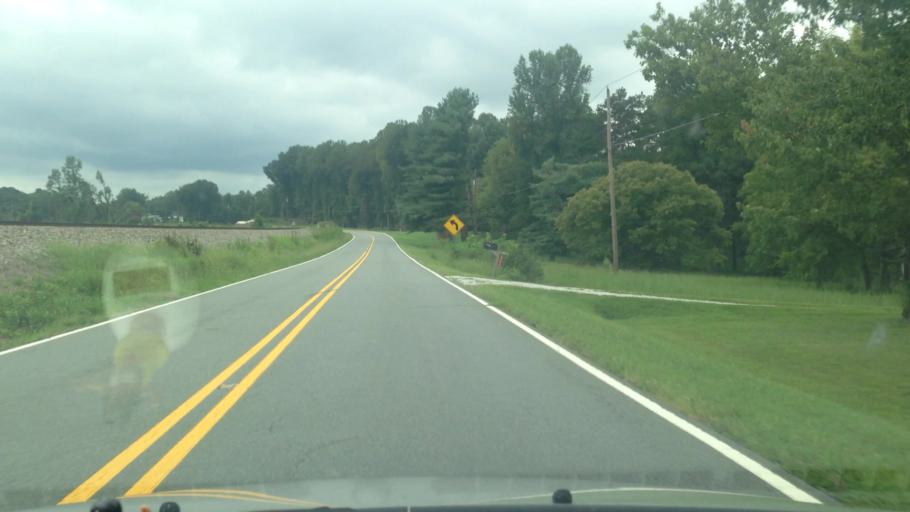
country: US
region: North Carolina
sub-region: Stokes County
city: Walnut Cove
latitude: 36.2486
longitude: -80.1520
